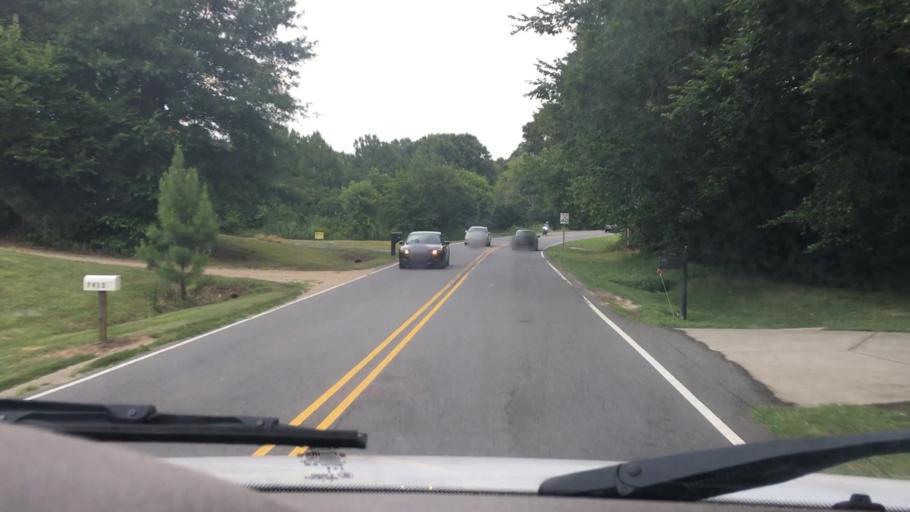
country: US
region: North Carolina
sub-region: Mecklenburg County
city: Huntersville
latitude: 35.4069
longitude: -80.8937
